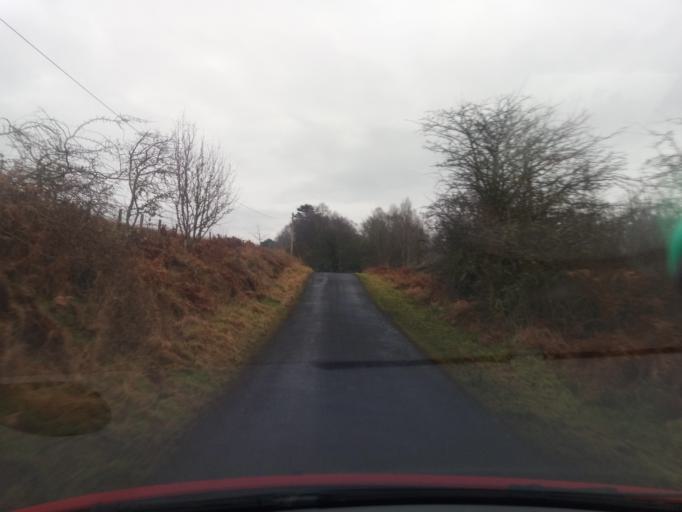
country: GB
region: England
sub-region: Northumberland
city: Rochester
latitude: 55.1772
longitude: -2.4296
